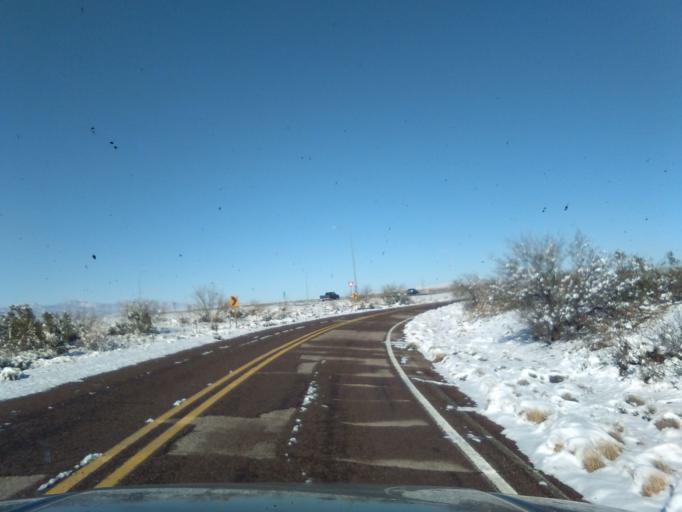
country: US
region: New Mexico
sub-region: Sierra County
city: Elephant Butte
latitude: 33.6224
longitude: -107.1365
